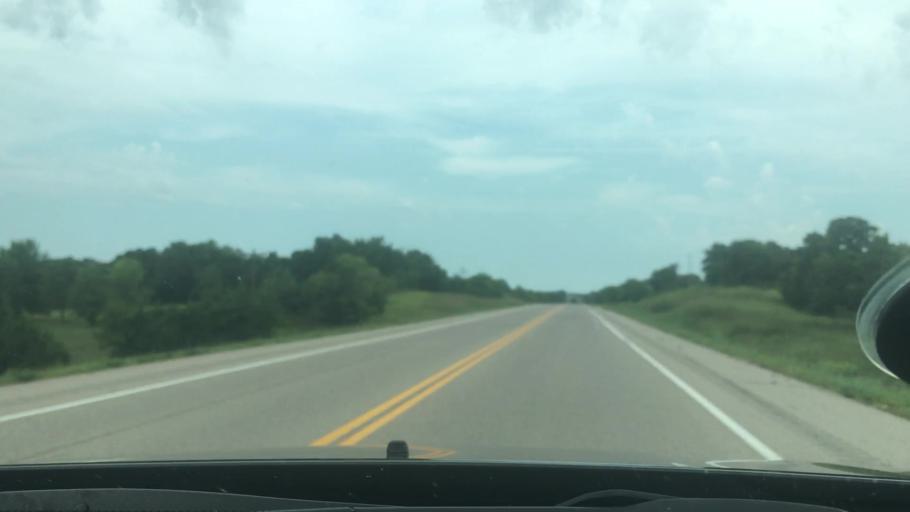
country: US
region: Oklahoma
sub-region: Seminole County
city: Konawa
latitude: 34.9973
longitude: -96.6790
